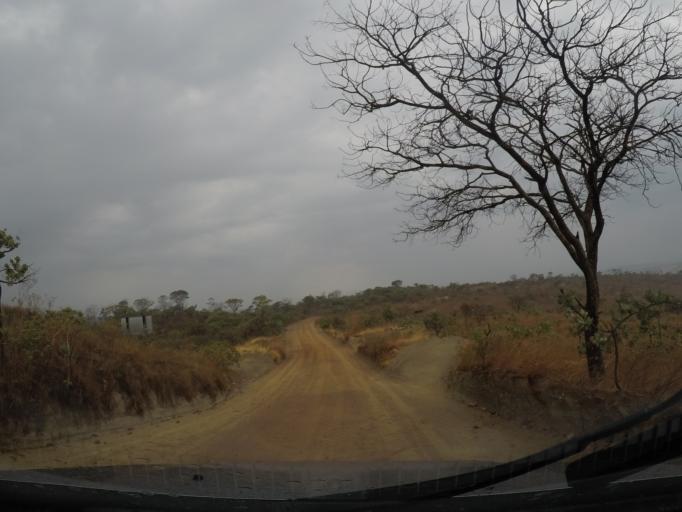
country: BR
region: Goias
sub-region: Pirenopolis
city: Pirenopolis
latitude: -15.8252
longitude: -48.9063
